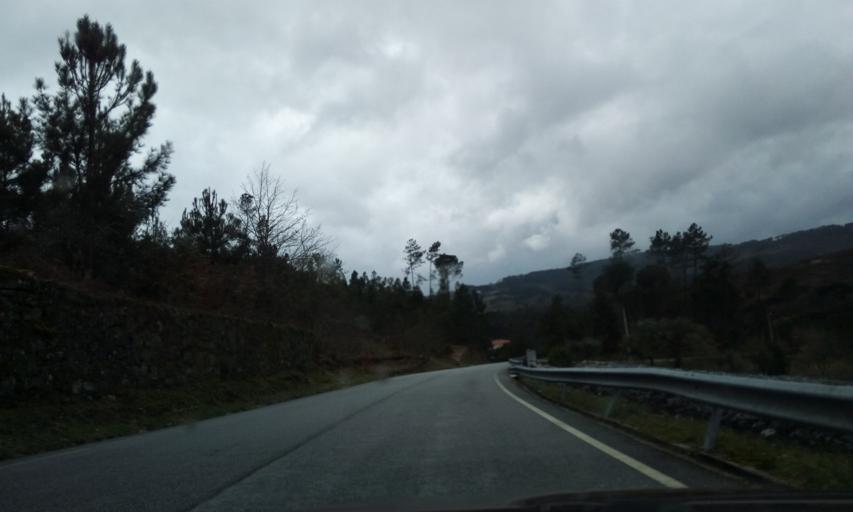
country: PT
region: Viseu
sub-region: Viseu
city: Rio de Loba
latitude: 40.6051
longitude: -7.8624
